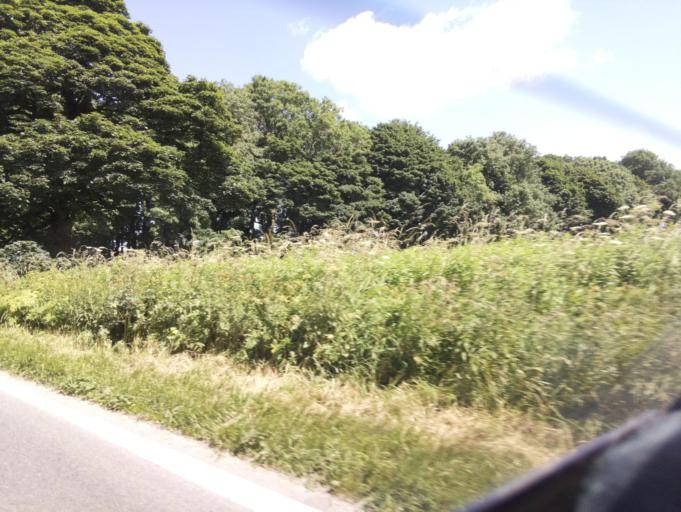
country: GB
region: England
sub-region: Derbyshire
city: Ashbourne
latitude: 53.1206
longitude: -1.7524
